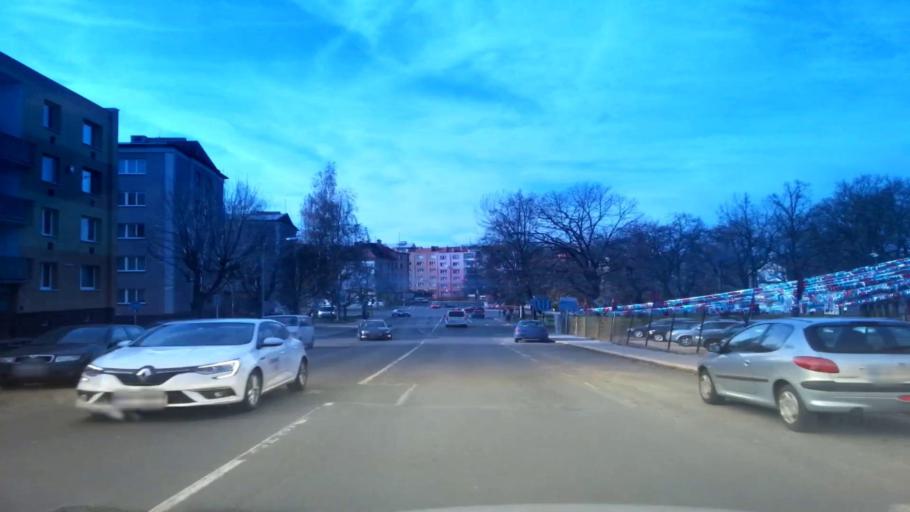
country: CZ
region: Karlovarsky
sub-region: Okres Cheb
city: Cheb
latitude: 50.0775
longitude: 12.3776
